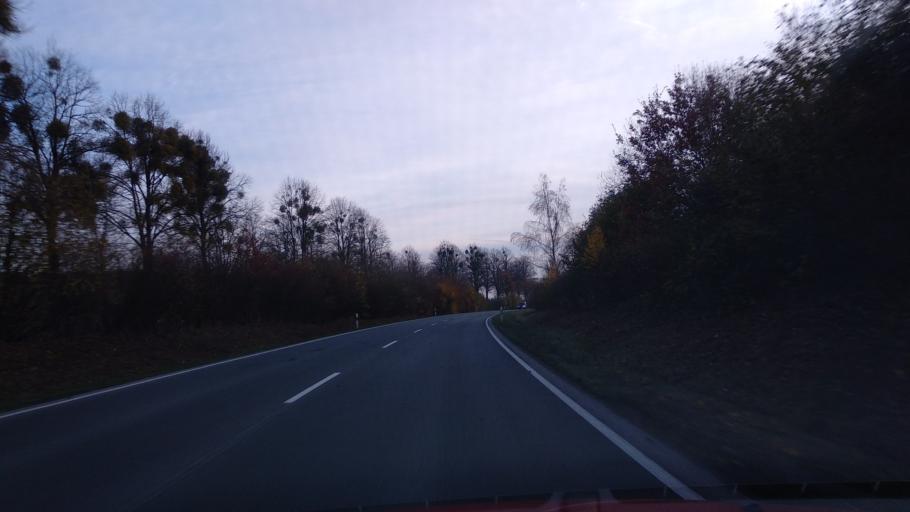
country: DE
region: Lower Saxony
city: Furstenberg
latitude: 51.7034
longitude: 9.3844
